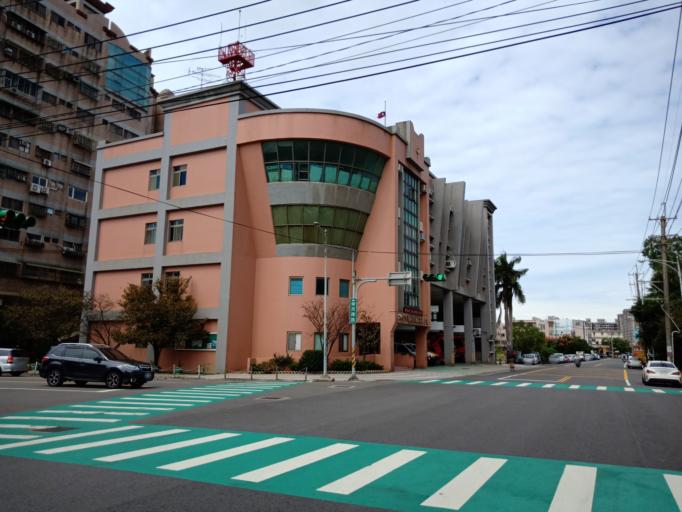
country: TW
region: Taiwan
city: Daxi
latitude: 24.9397
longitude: 121.2563
